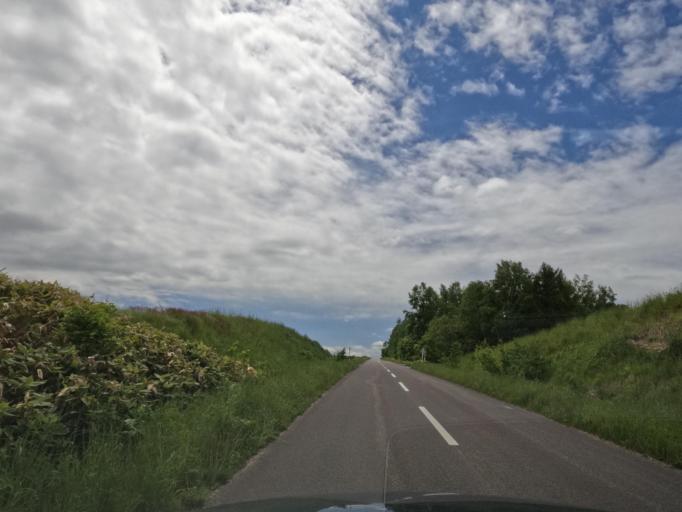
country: JP
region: Hokkaido
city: Shimo-furano
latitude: 43.5102
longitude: 142.4214
